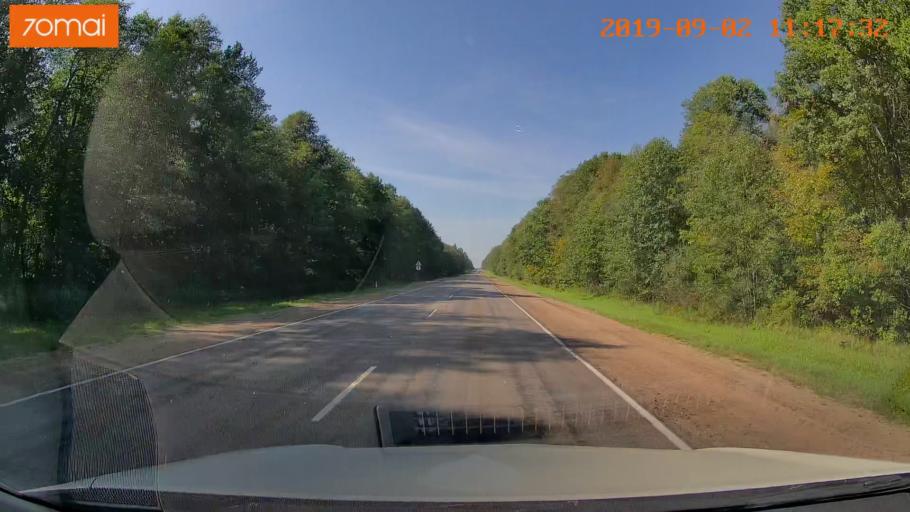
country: RU
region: Smolensk
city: Yekimovichi
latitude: 54.0610
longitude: 33.1163
